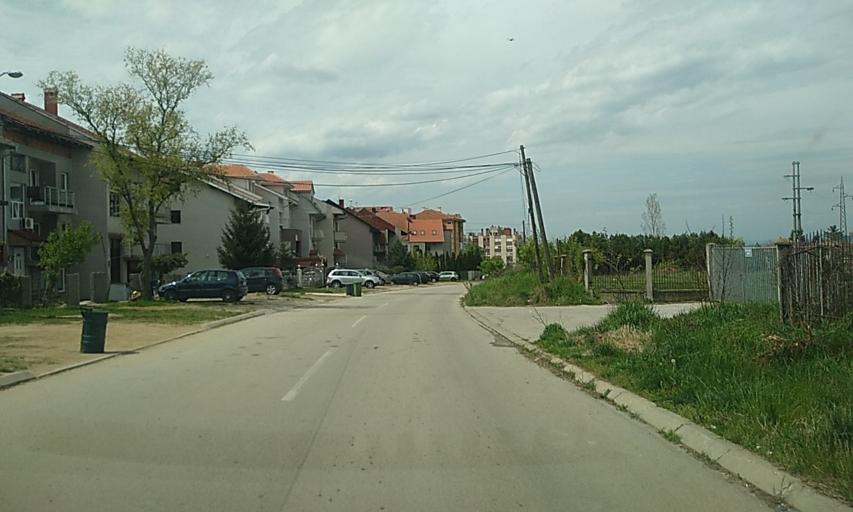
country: RS
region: Central Serbia
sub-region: Nisavski Okrug
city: Nis
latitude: 43.3107
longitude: 21.8624
